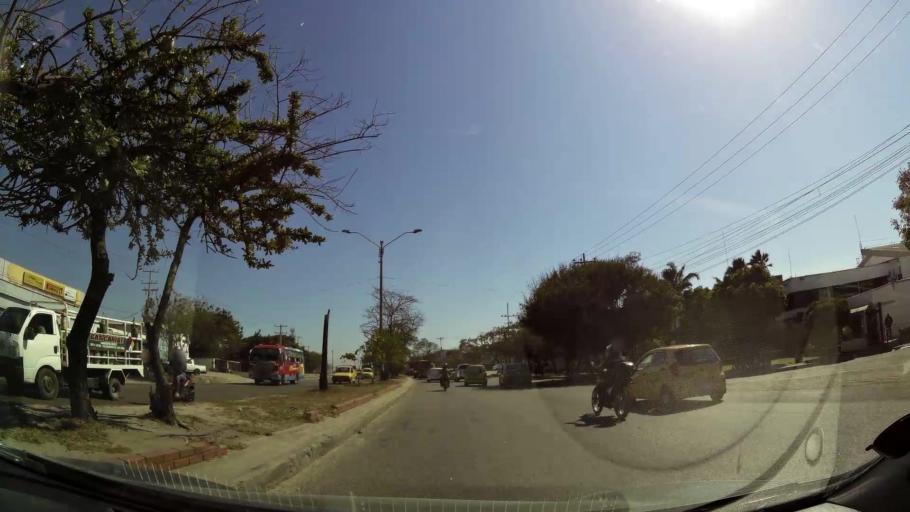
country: CO
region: Atlantico
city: Barranquilla
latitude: 10.9539
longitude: -74.7867
